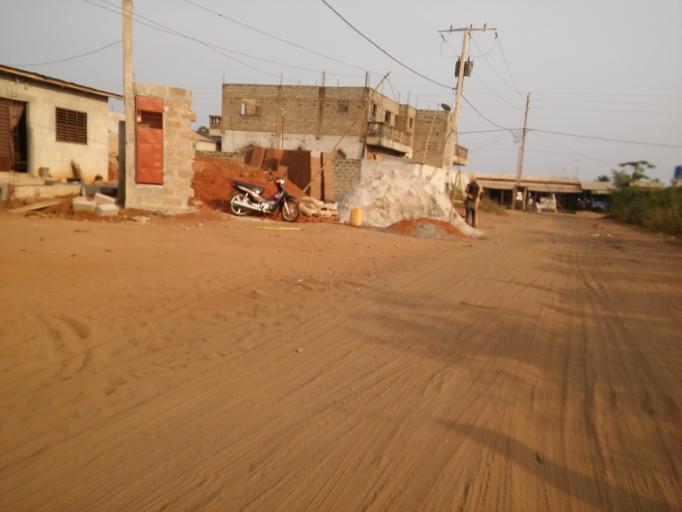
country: BJ
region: Atlantique
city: Abomey-Calavi
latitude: 6.4182
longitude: 2.3346
